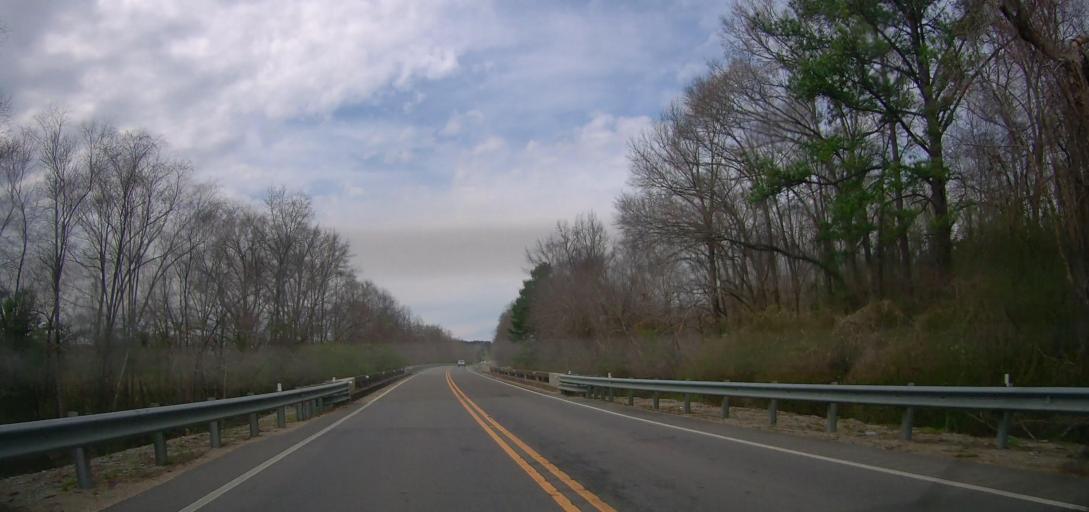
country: US
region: Alabama
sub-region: Marion County
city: Guin
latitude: 33.9956
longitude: -87.9294
